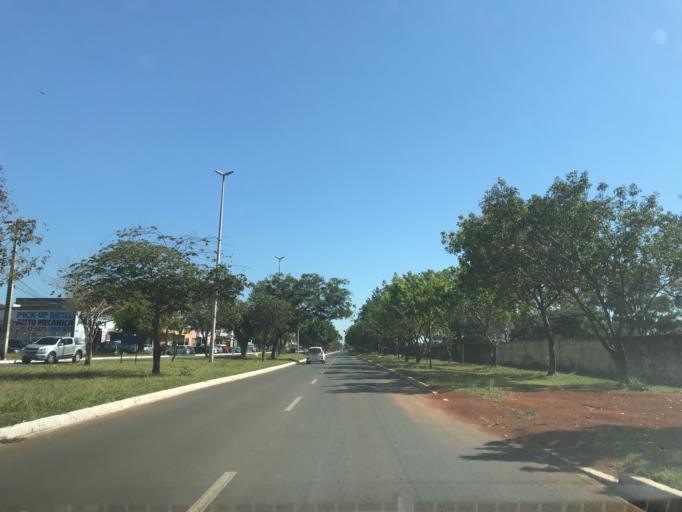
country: BR
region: Federal District
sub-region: Brasilia
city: Brasilia
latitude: -15.8066
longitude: -48.0897
